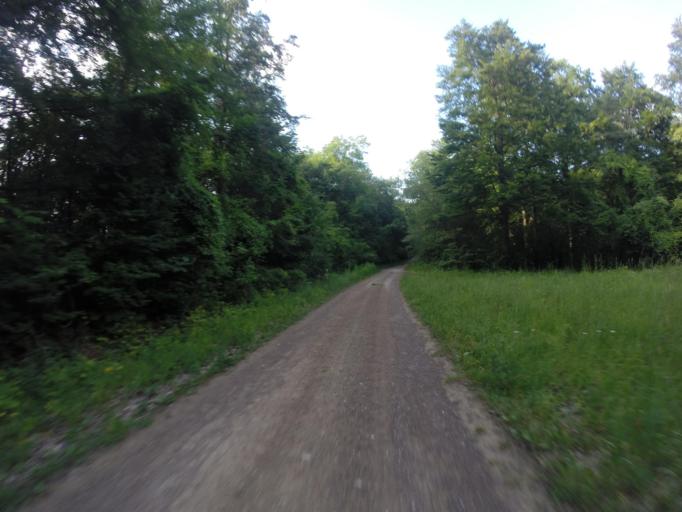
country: DE
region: Thuringia
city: Grosslobichau
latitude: 50.9454
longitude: 11.6692
